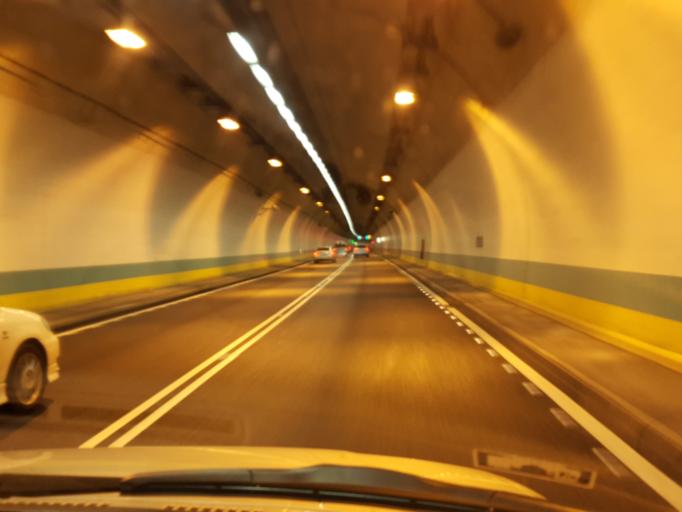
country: TW
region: Taiwan
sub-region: Keelung
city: Keelung
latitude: 24.9498
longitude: 121.7008
